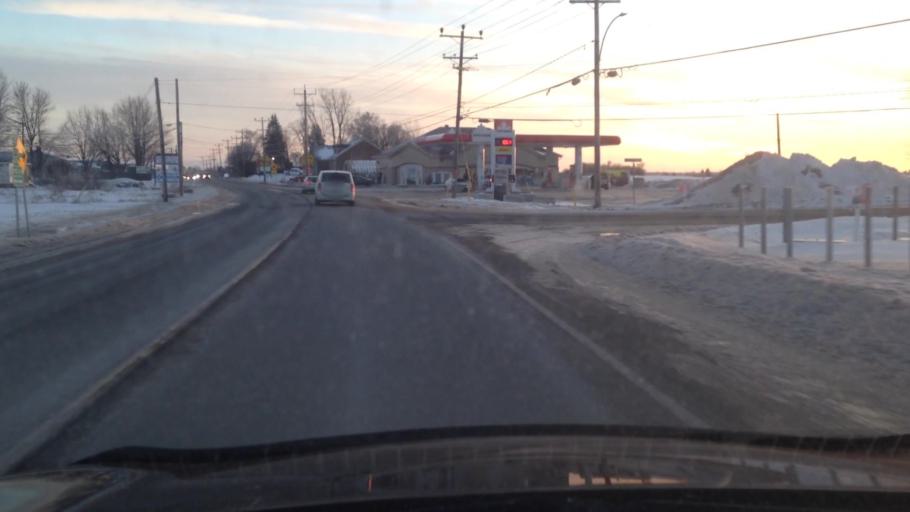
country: CA
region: Quebec
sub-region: Lanaudiere
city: Saint-Lin-Laurentides
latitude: 45.8893
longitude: -73.7579
